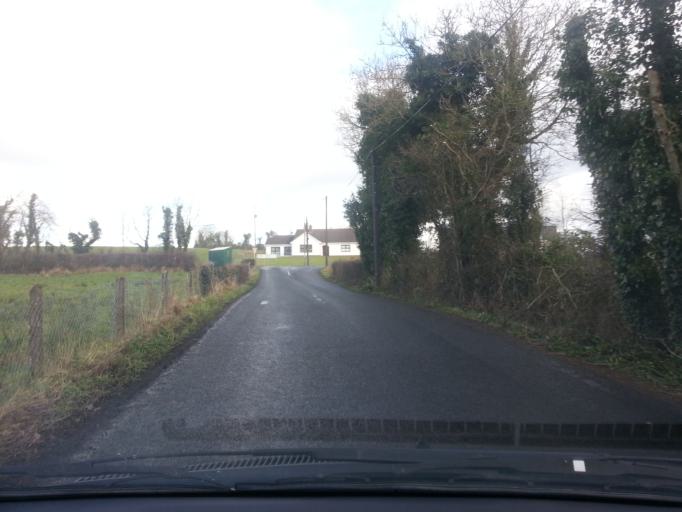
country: GB
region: Northern Ireland
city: Lisnaskea
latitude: 54.2777
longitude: -7.5105
